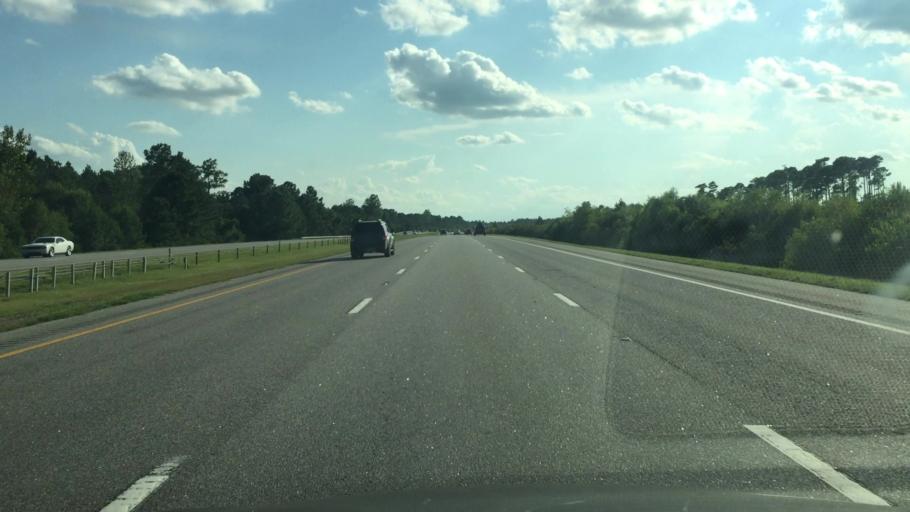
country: US
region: South Carolina
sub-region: Horry County
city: Myrtle Beach
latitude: 33.7752
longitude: -78.8168
